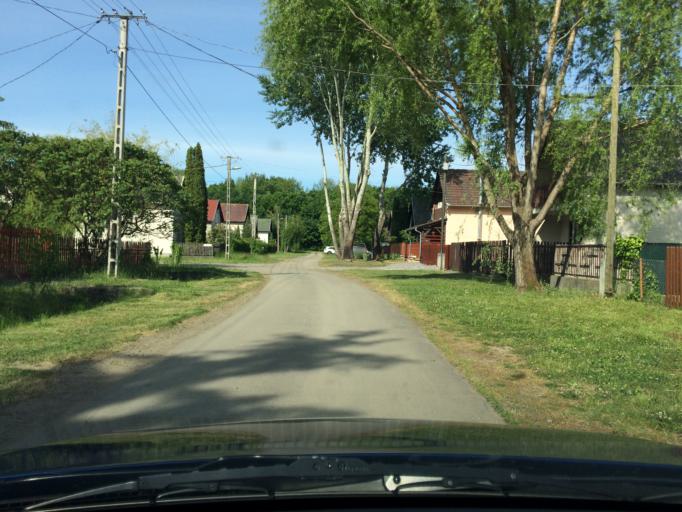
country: HU
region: Szabolcs-Szatmar-Bereg
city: Tiszavasvari
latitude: 47.9523
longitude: 21.3493
